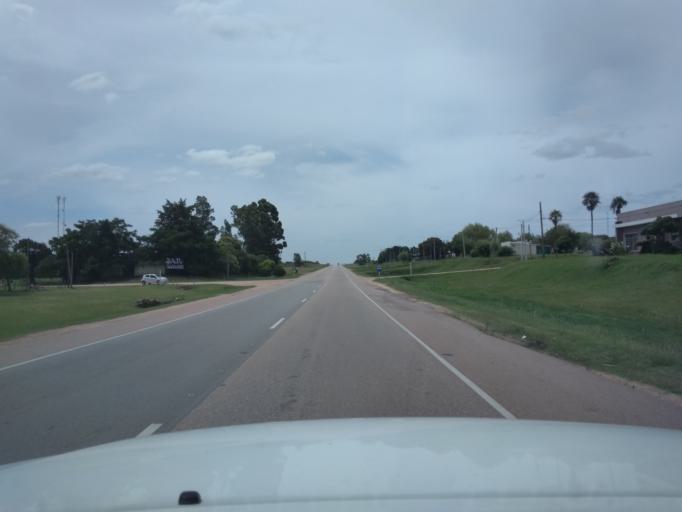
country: UY
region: Canelones
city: Canelones
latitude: -34.4958
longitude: -56.2819
